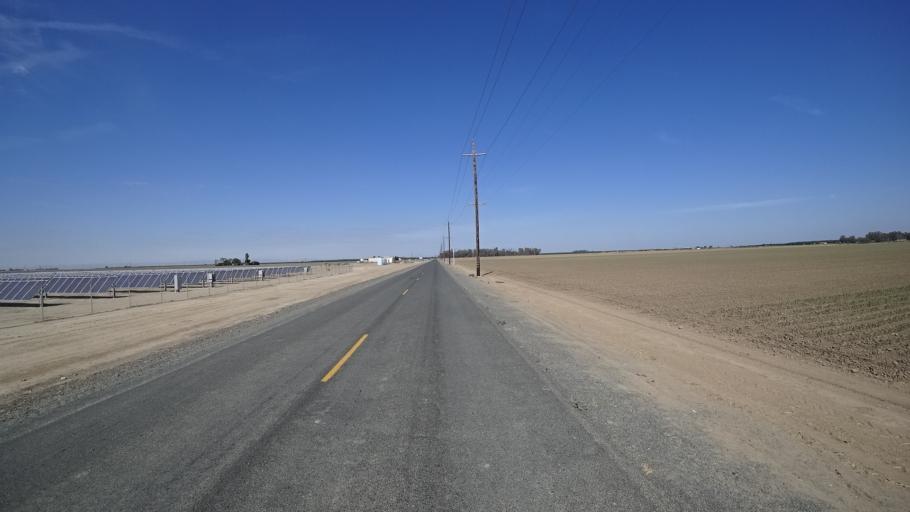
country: US
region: California
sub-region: Kings County
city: Home Garden
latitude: 36.2548
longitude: -119.6663
